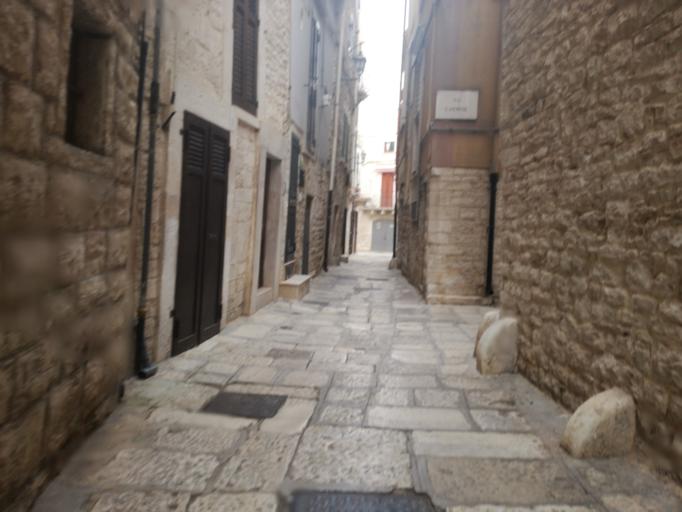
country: IT
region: Apulia
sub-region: Provincia di Bari
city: Ruvo di Puglia
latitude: 41.1164
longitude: 16.4863
